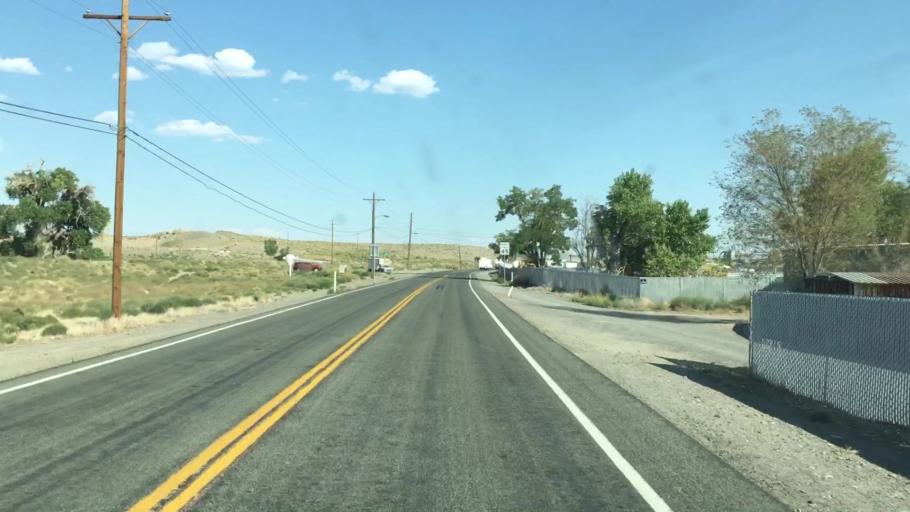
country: US
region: Nevada
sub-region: Lyon County
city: Fernley
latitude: 39.6308
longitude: -119.2794
